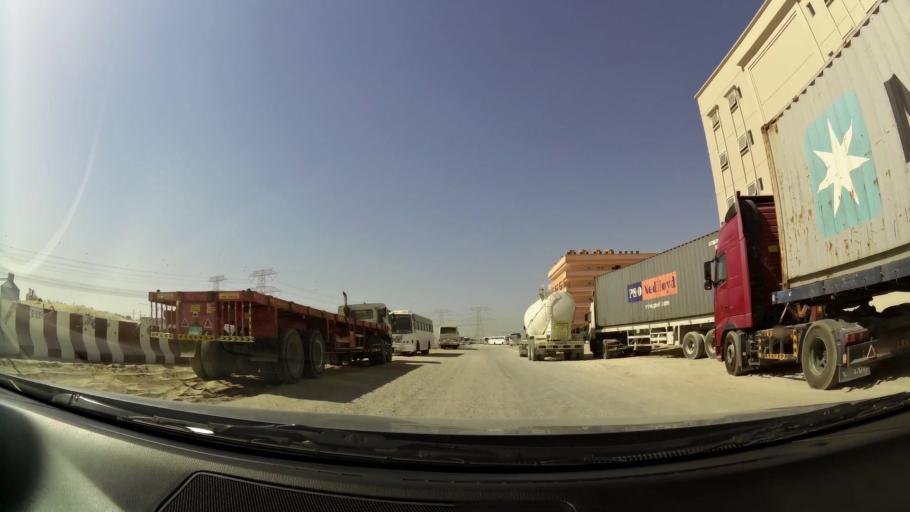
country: AE
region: Dubai
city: Dubai
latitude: 24.9988
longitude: 55.1413
